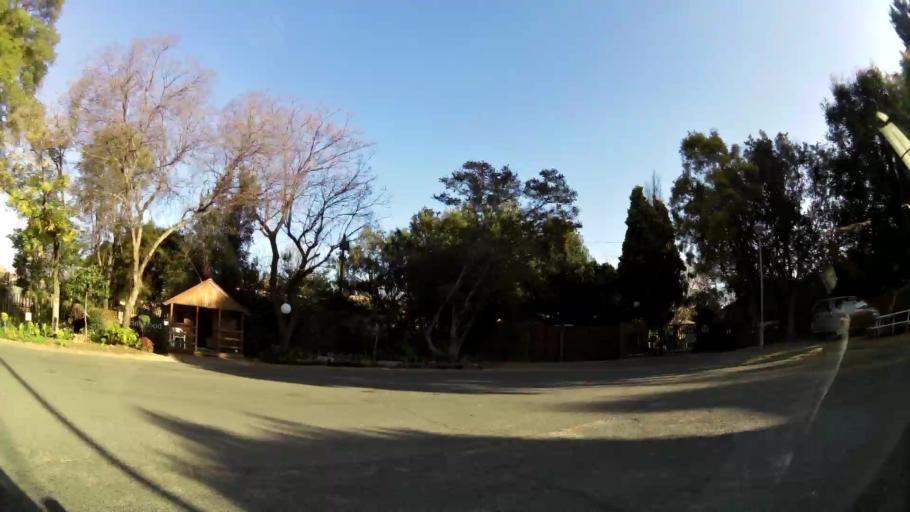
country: ZA
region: Gauteng
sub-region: City of Johannesburg Metropolitan Municipality
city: Modderfontein
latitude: -26.0910
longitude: 28.0590
